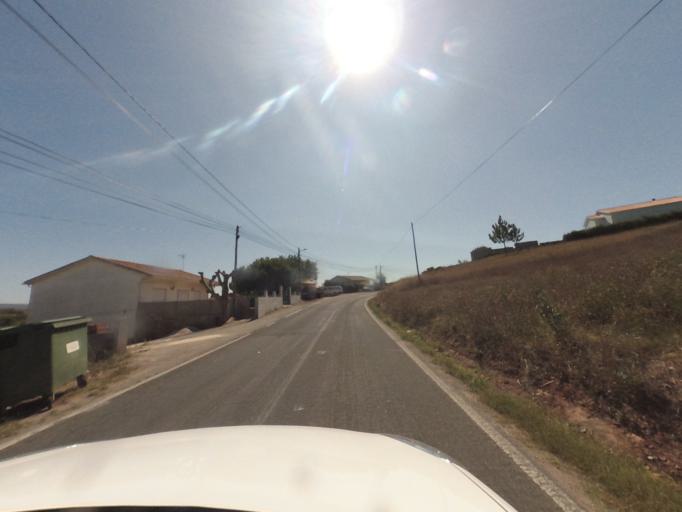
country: PT
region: Leiria
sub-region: Alcobaca
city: Turquel
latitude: 39.4869
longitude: -8.9813
